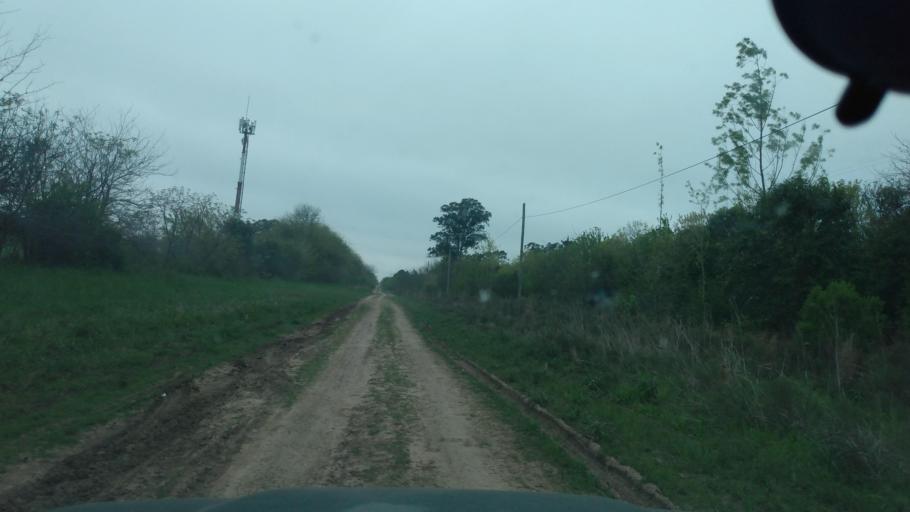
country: AR
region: Buenos Aires
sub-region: Partido de Lujan
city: Lujan
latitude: -34.5439
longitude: -59.2127
